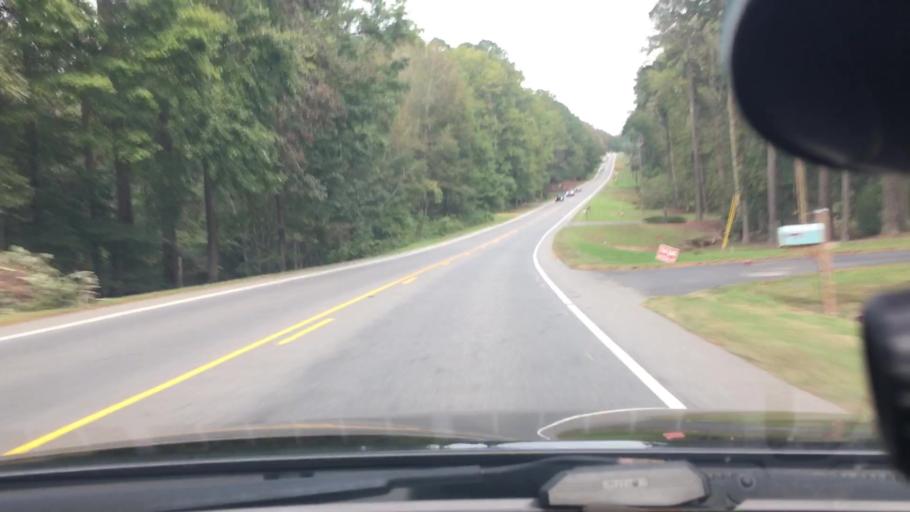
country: US
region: North Carolina
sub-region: Montgomery County
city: Troy
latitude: 35.3621
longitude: -79.8759
